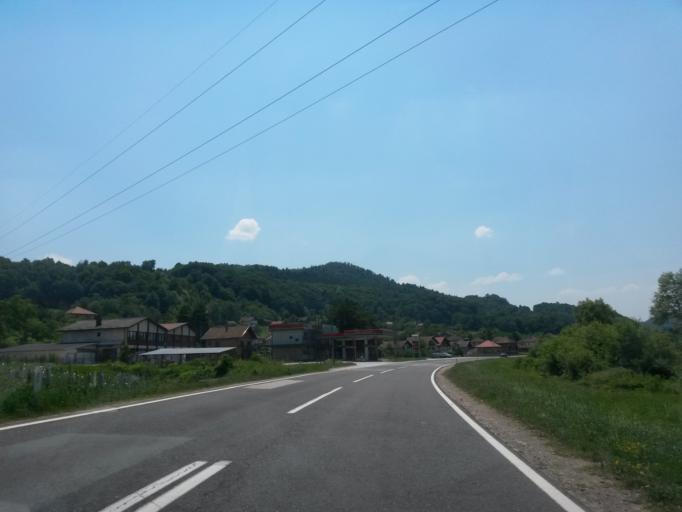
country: BA
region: Federation of Bosnia and Herzegovina
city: Maglaj
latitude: 44.5251
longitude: 18.0948
